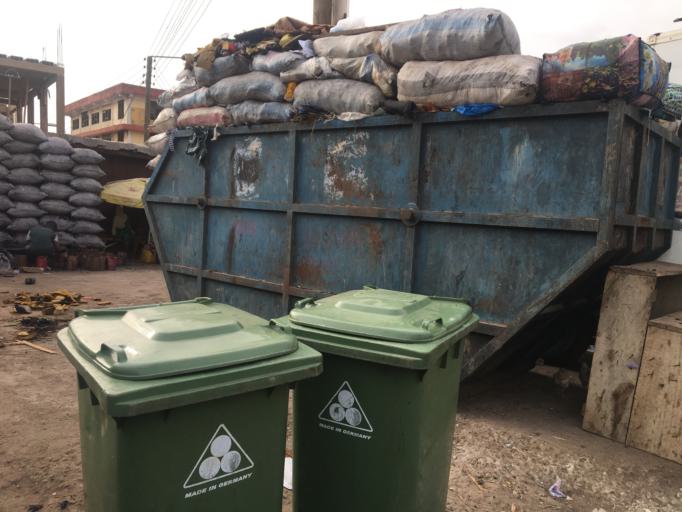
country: GH
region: Greater Accra
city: Accra
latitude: 5.5839
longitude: -0.1982
